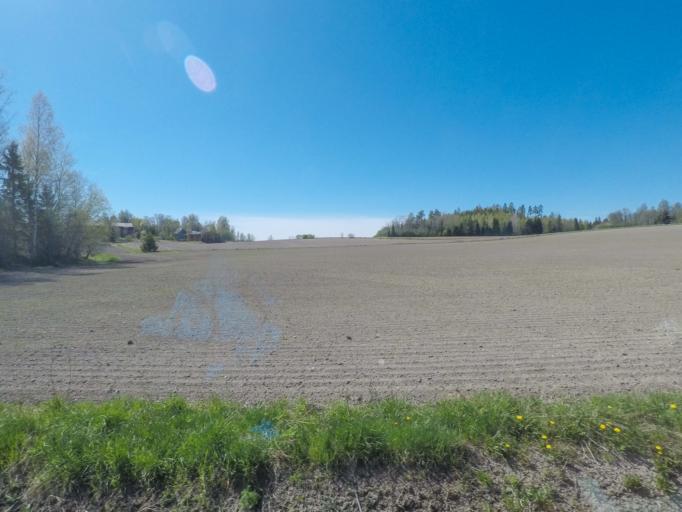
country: FI
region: Uusimaa
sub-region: Helsinki
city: Sammatti
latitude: 60.4788
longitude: 23.8286
